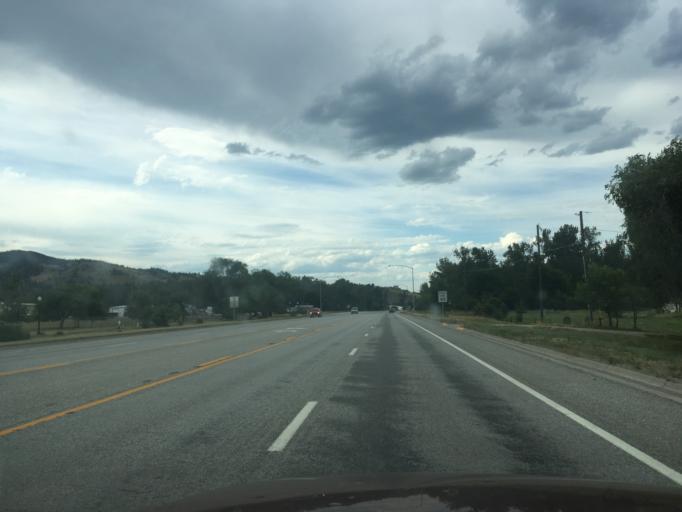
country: US
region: Montana
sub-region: Missoula County
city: Lolo
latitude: 46.7457
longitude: -114.0822
